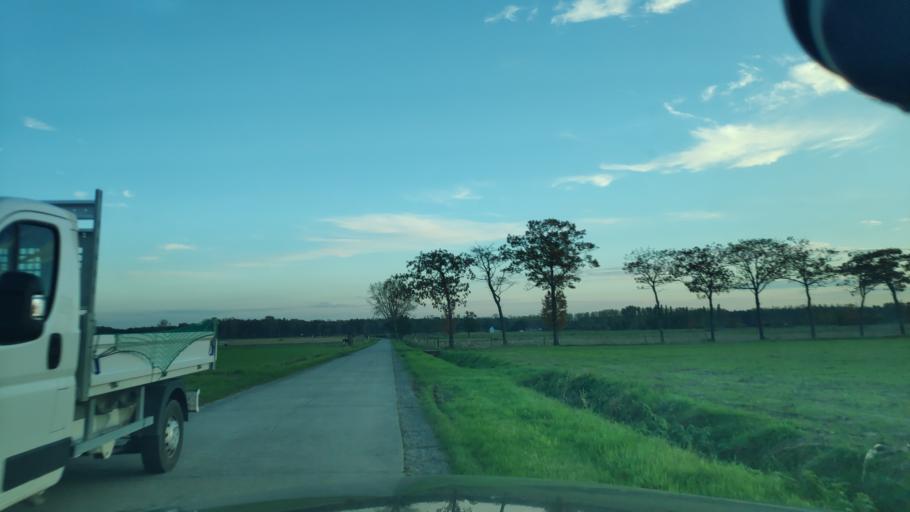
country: BE
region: Flanders
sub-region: Provincie Oost-Vlaanderen
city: Eeklo
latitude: 51.1486
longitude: 3.5018
